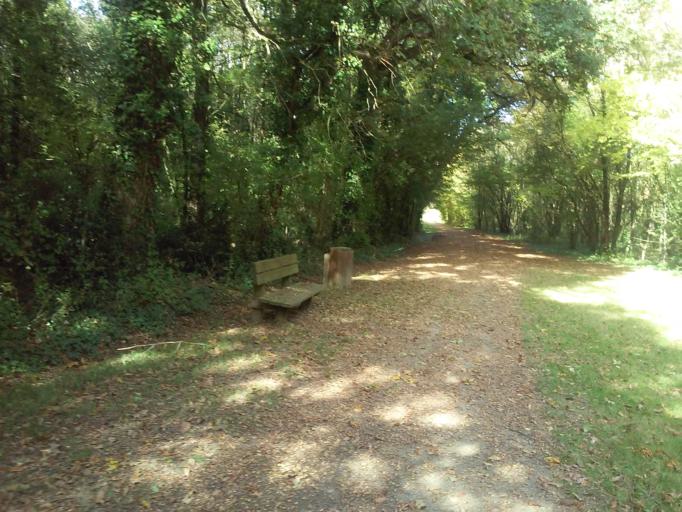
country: FR
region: Pays de la Loire
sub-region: Departement de la Vendee
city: Saint-Andre-Treize-Voies
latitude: 46.8757
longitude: -1.4009
